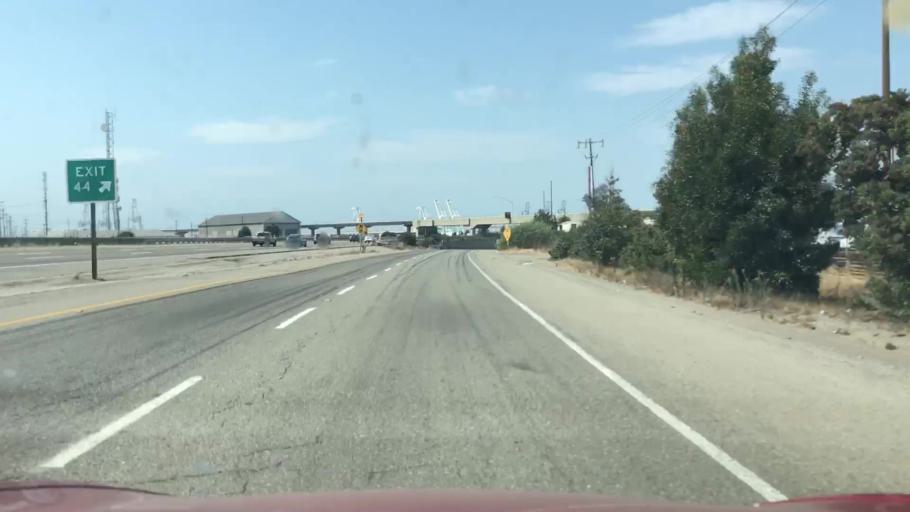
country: US
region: California
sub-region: Alameda County
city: Emeryville
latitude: 37.8059
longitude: -122.3030
